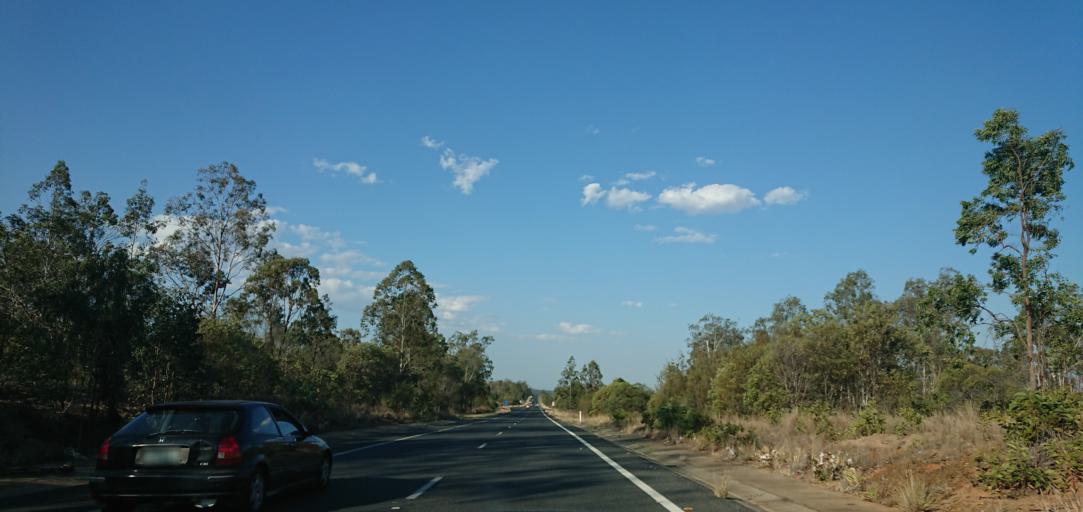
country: AU
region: Queensland
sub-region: Lockyer Valley
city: Gatton
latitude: -27.5499
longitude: 152.2175
